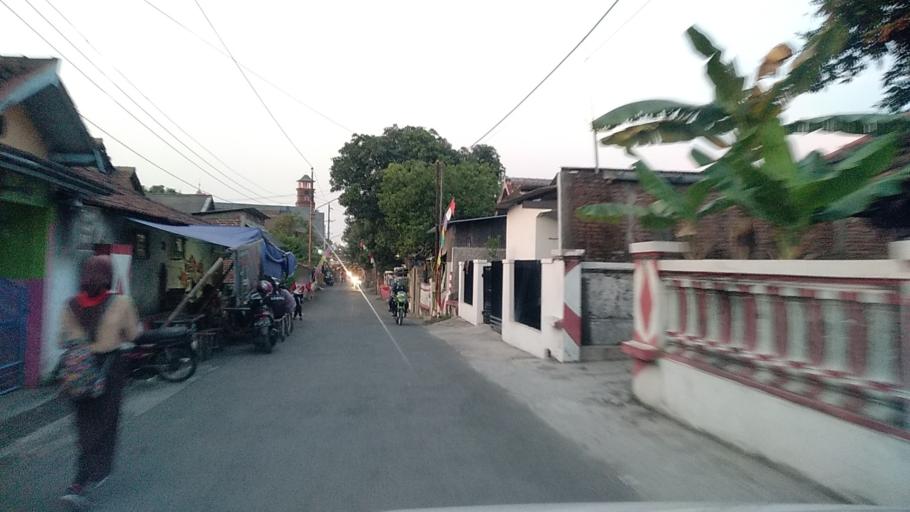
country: ID
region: Central Java
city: Semarang
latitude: -6.9769
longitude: 110.3312
